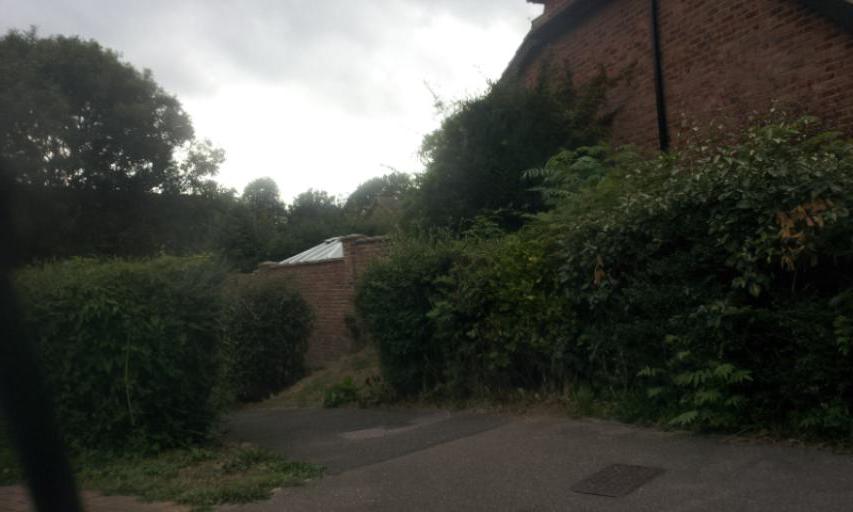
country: GB
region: England
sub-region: Kent
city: Tonbridge
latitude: 51.2053
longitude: 0.2831
